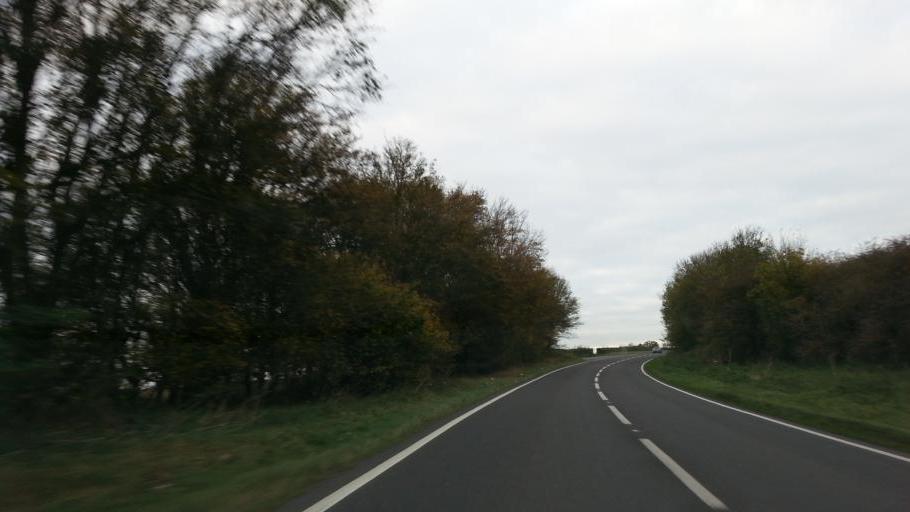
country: GB
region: England
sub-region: District of Rutland
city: Ketton
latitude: 52.6067
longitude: -0.5364
